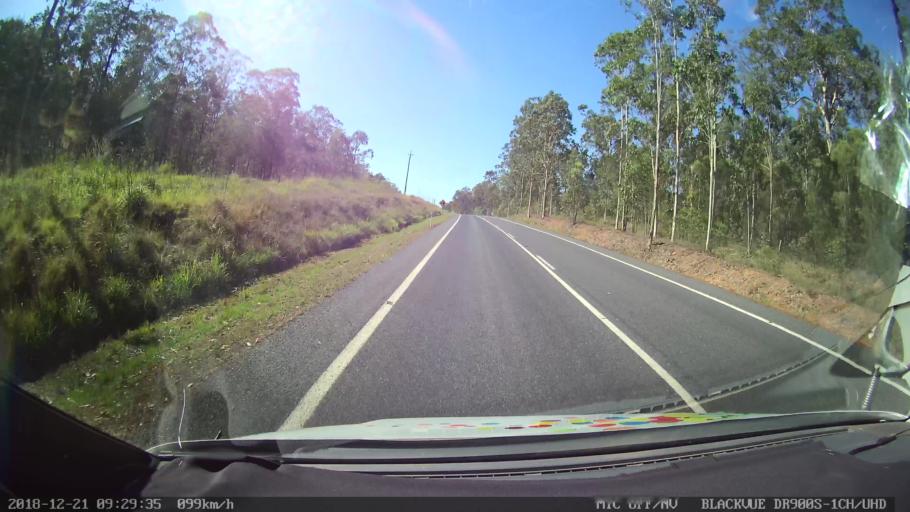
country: AU
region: New South Wales
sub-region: Clarence Valley
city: Maclean
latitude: -29.4338
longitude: 152.9897
